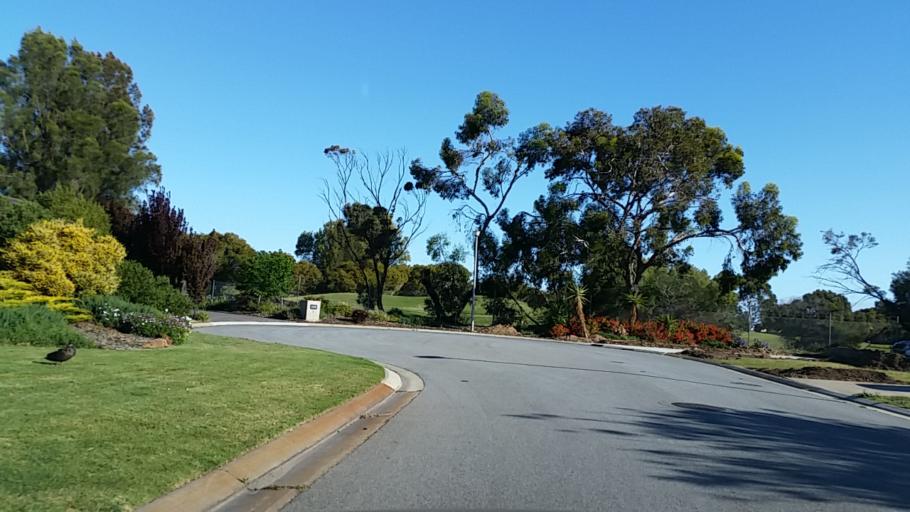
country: AU
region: South Australia
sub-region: Charles Sturt
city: West Lakes Shore
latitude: -34.8684
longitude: 138.4961
